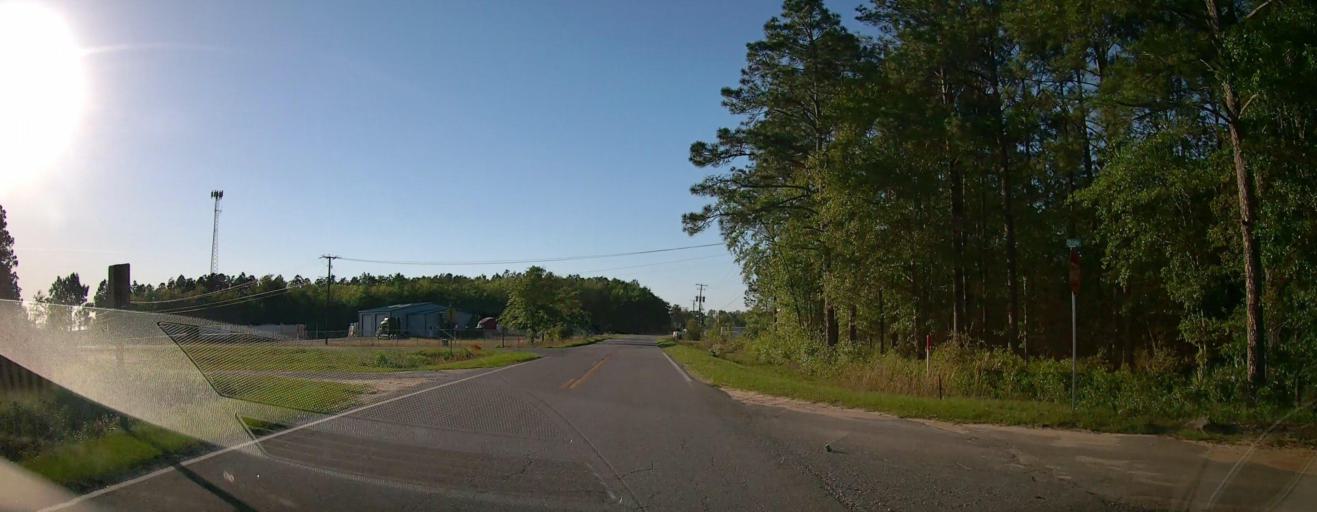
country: US
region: Georgia
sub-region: Ben Hill County
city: Fitzgerald
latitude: 31.6918
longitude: -83.2174
